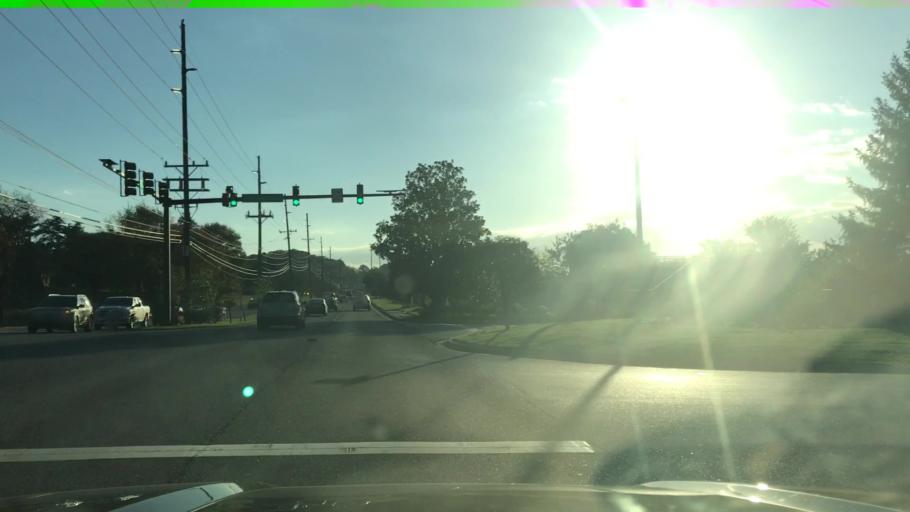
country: US
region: Tennessee
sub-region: Williamson County
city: Brentwood
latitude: 36.0377
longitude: -86.7950
